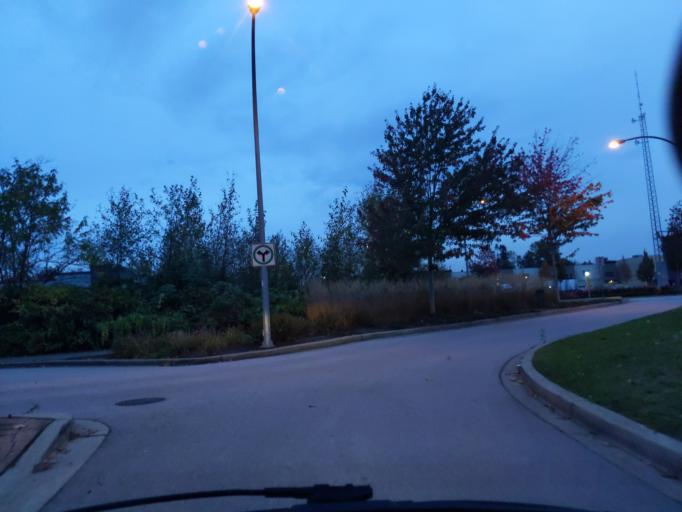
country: CA
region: British Columbia
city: Walnut Grove
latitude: 49.1816
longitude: -122.6601
